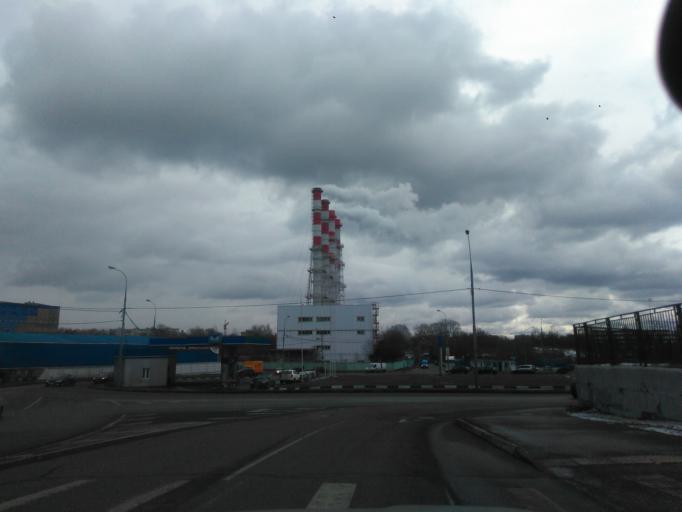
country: RU
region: Moscow
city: Strogino
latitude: 55.8328
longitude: 37.4049
